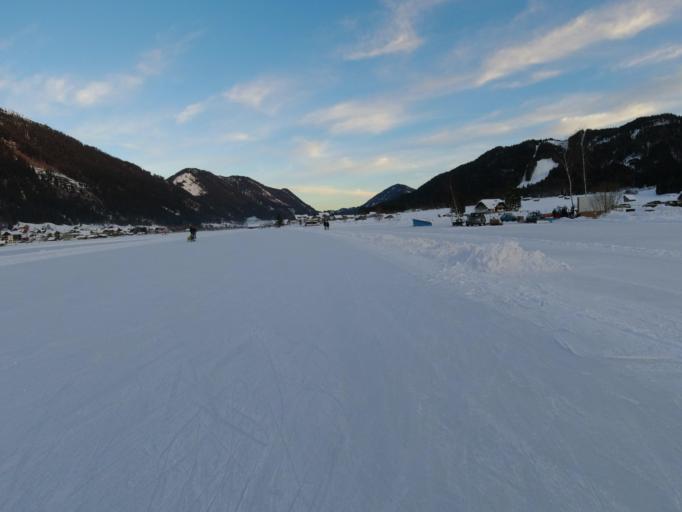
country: AT
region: Carinthia
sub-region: Politischer Bezirk Spittal an der Drau
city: Steinfeld
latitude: 46.7145
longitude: 13.2847
